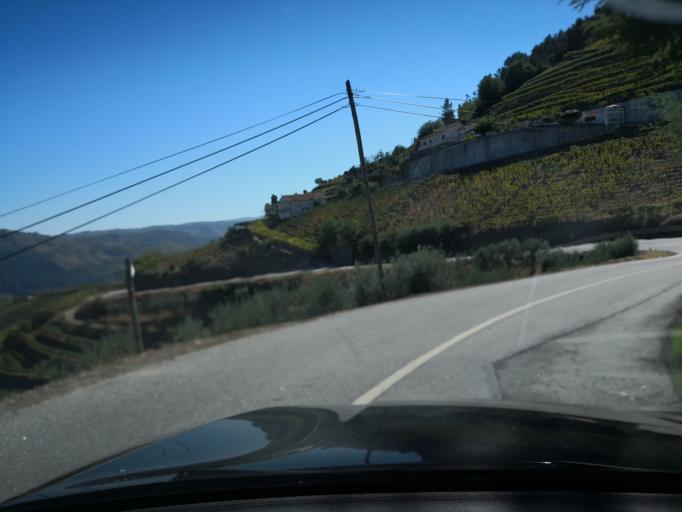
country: PT
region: Vila Real
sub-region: Santa Marta de Penaguiao
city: Santa Marta de Penaguiao
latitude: 41.2270
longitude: -7.7880
